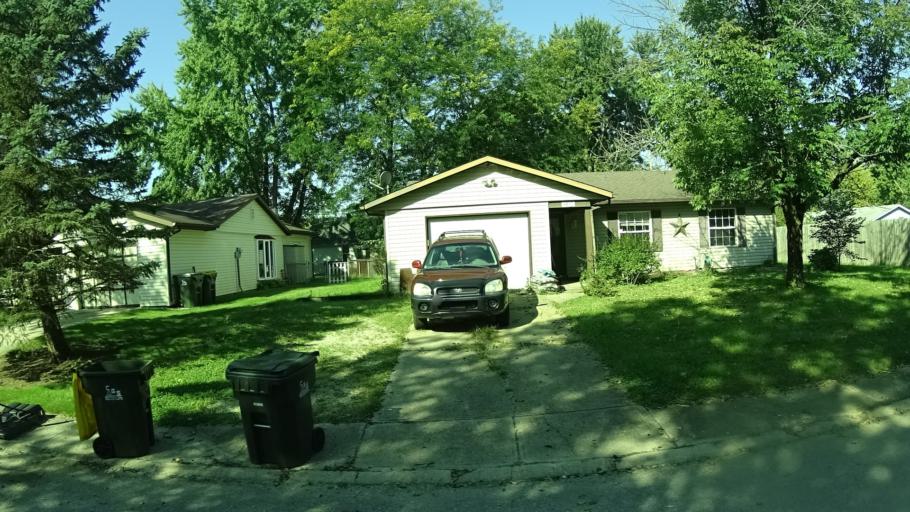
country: US
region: Indiana
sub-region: Madison County
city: Lapel
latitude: 40.0729
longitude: -85.8467
